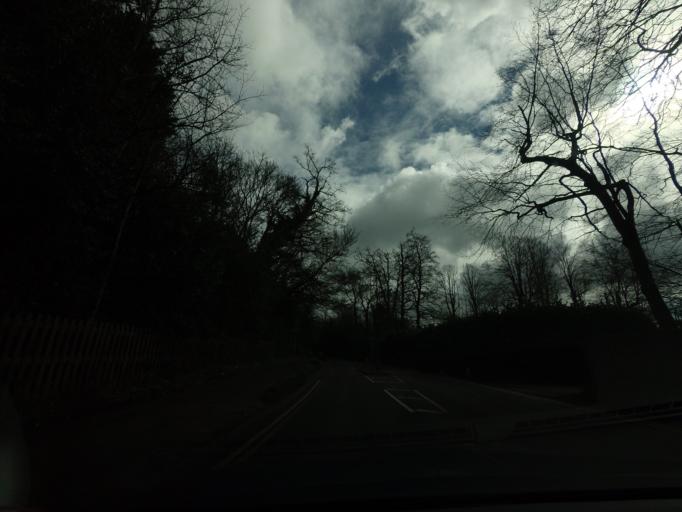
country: GB
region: England
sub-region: Kent
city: Kemsing
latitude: 51.2877
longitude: 0.2246
